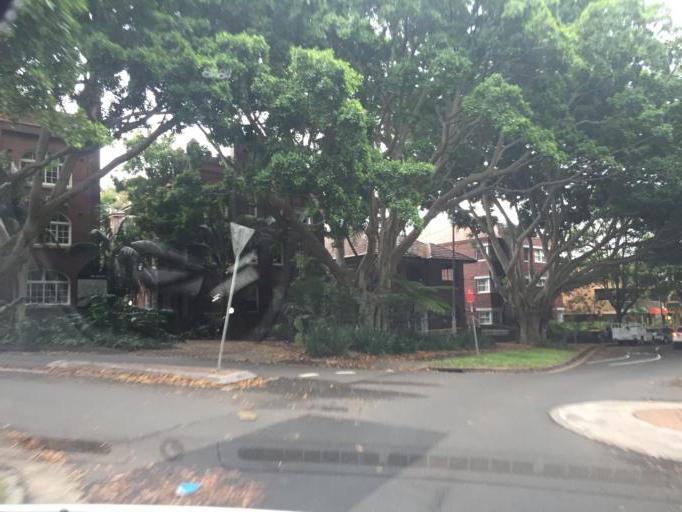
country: AU
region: New South Wales
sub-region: Woollahra
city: Bellevue Hill
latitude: -33.8762
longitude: 151.2606
